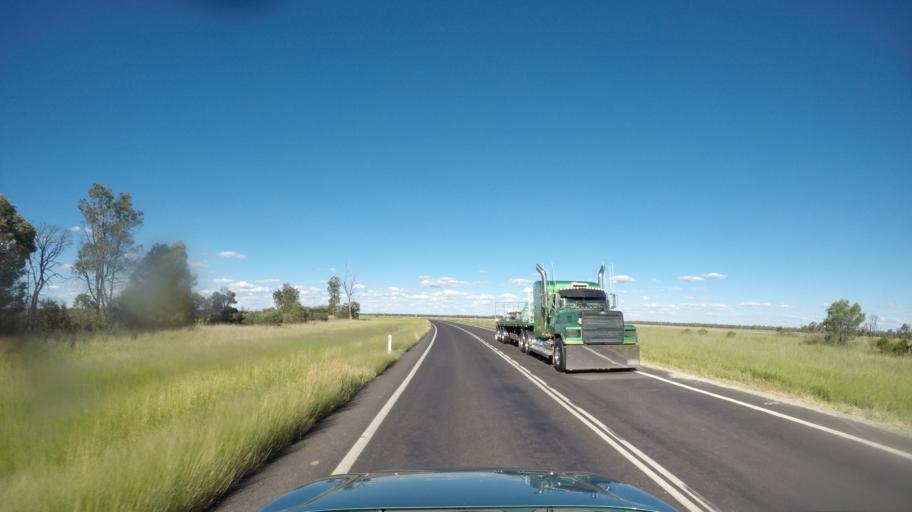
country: AU
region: Queensland
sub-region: Goondiwindi
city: Goondiwindi
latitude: -28.1515
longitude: 150.6810
